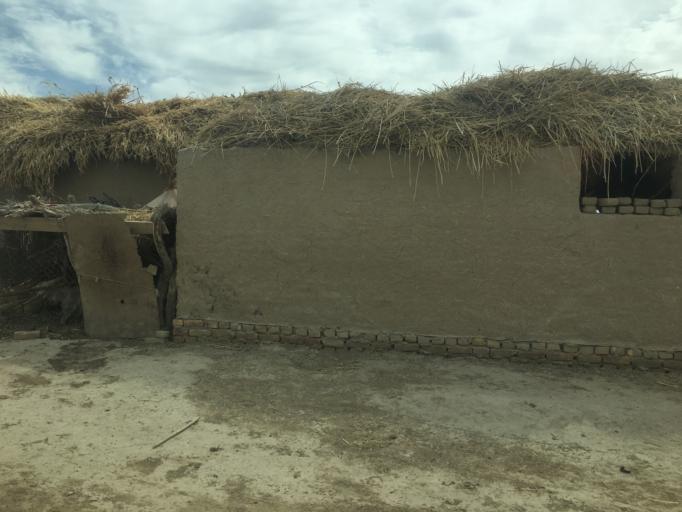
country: TM
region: Dasoguz
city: Tagta
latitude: 41.6125
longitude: 59.8167
